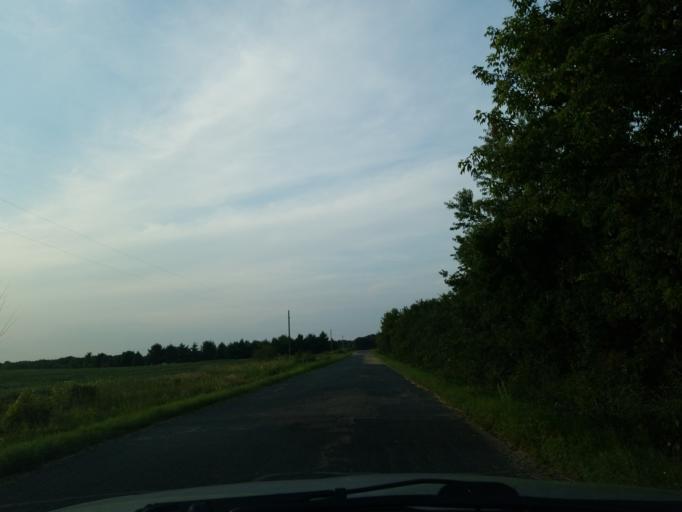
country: US
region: Minnesota
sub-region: Washington County
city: Stillwater
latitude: 45.0661
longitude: -92.7609
